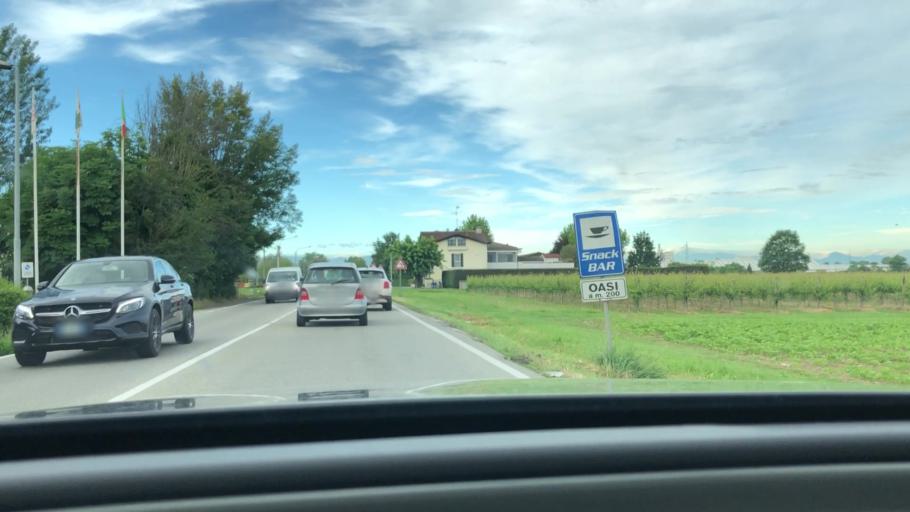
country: IT
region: Emilia-Romagna
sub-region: Provincia di Modena
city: San Damaso
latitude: 44.6064
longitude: 10.9339
